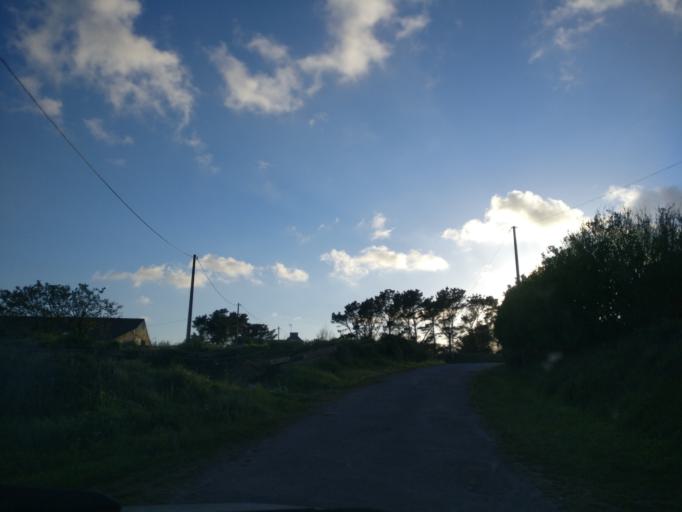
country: FR
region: Brittany
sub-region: Departement du Finistere
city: Lampaul-Plouarzel
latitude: 48.4665
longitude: -4.7445
